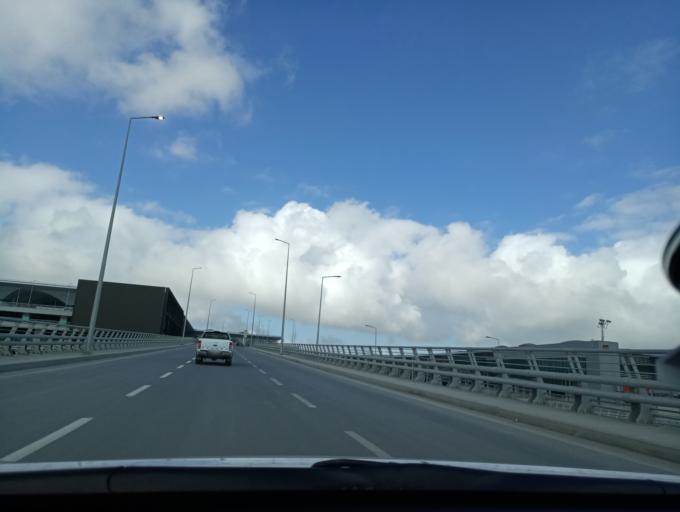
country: TR
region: Istanbul
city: Durusu
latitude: 41.2561
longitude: 28.7464
